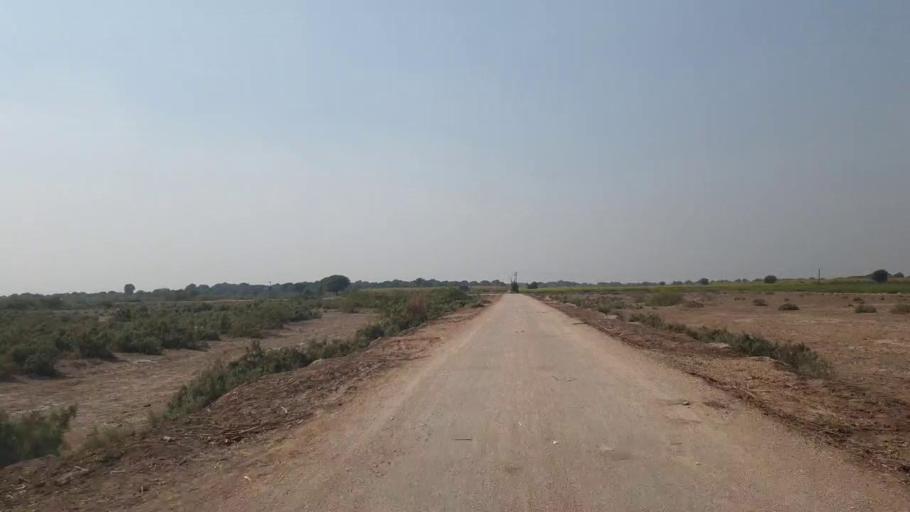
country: PK
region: Sindh
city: Chambar
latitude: 25.3812
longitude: 68.8827
